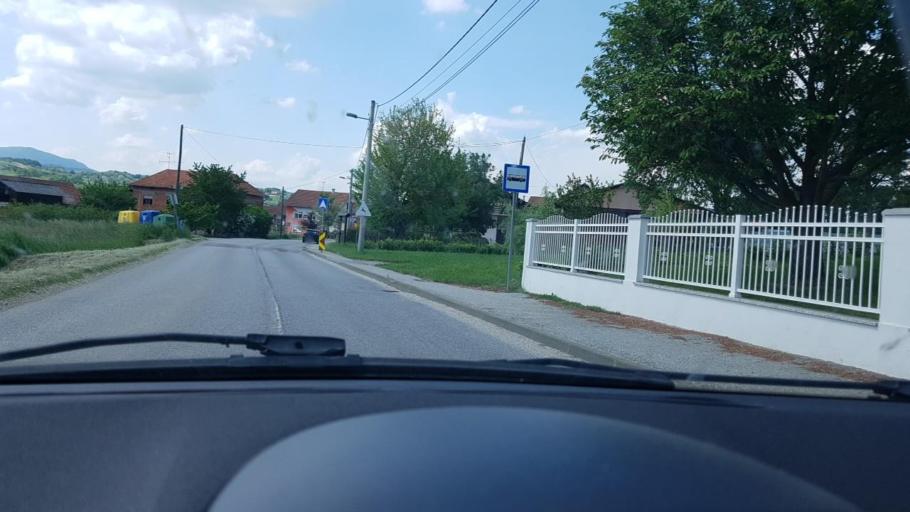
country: HR
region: Grad Zagreb
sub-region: Sesvete
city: Sesvete
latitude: 45.8946
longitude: 16.1687
